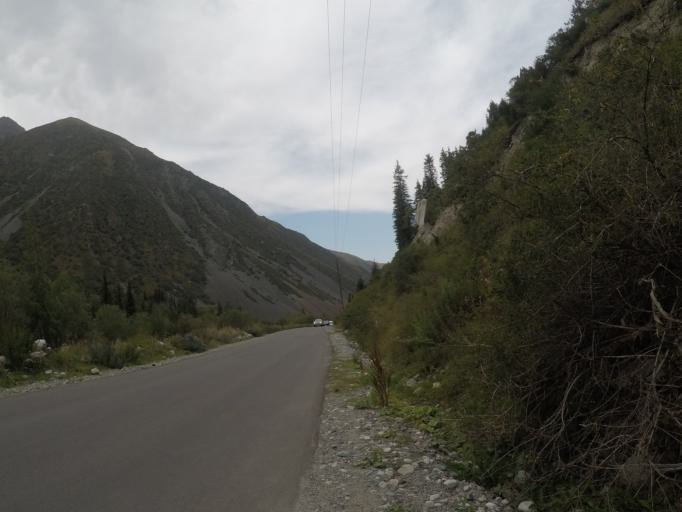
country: KG
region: Chuy
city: Bishkek
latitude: 42.5748
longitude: 74.4827
